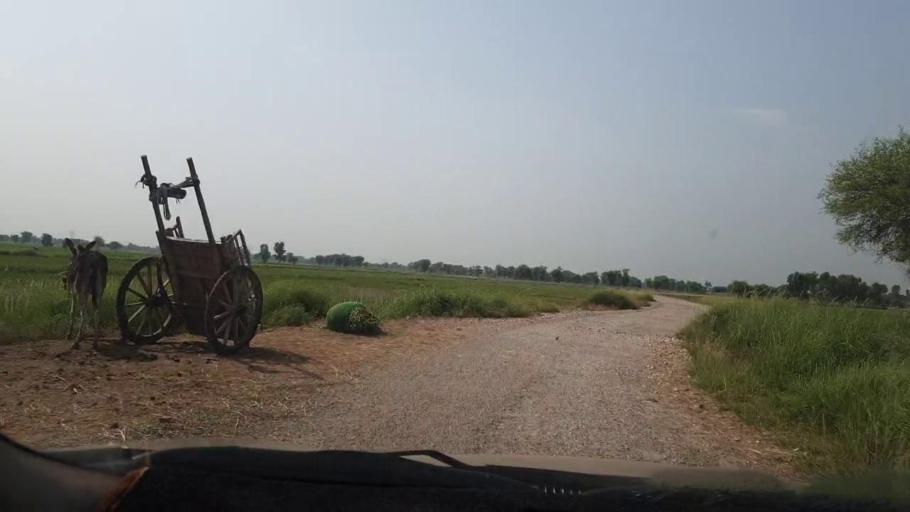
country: PK
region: Sindh
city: Goth Garelo
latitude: 27.4425
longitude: 68.0379
